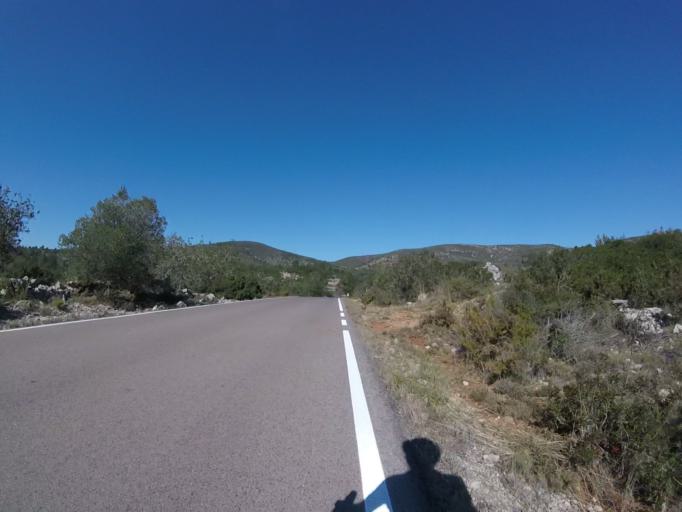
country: ES
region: Valencia
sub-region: Provincia de Castello
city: Santa Magdalena de Pulpis
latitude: 40.3780
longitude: 0.2700
